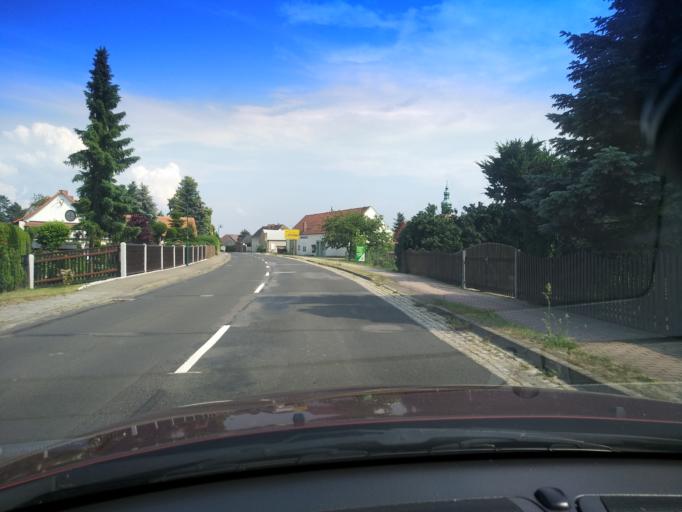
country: DE
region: Saxony
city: Klitten
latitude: 51.3496
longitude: 14.6013
